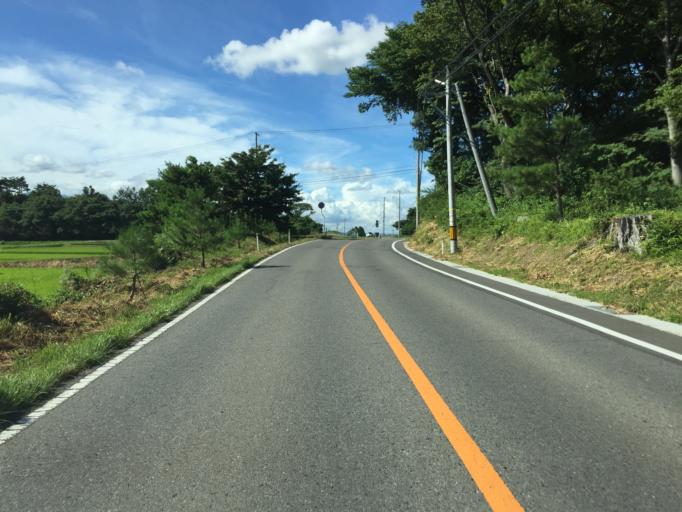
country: JP
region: Fukushima
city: Motomiya
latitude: 37.4659
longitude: 140.3902
